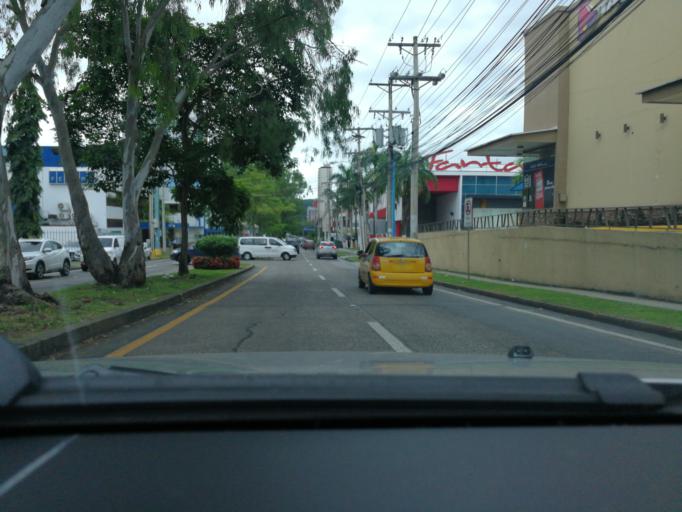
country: PA
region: Panama
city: Panama
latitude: 9.0071
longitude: -79.5346
